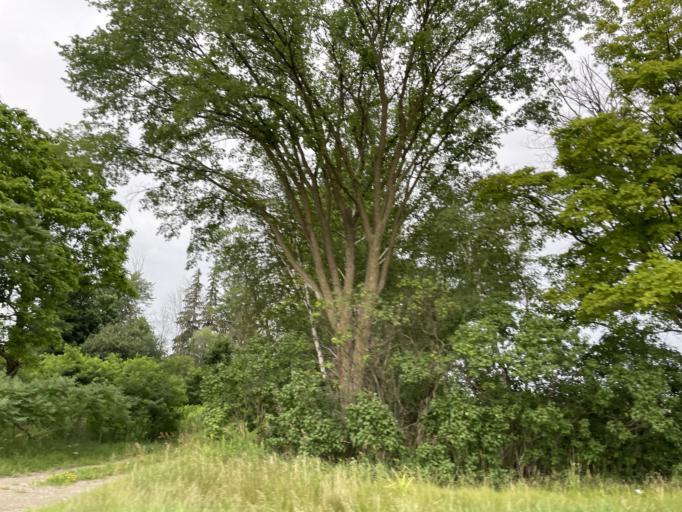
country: CA
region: Ontario
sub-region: Wellington County
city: Guelph
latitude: 43.5429
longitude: -80.3203
